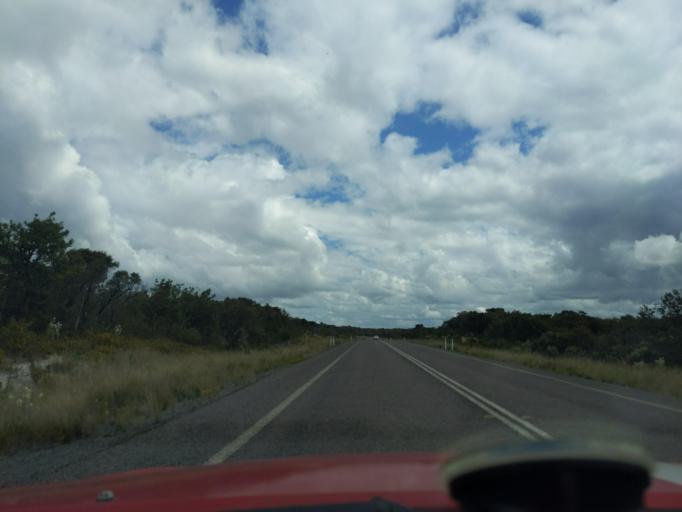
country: AU
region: New South Wales
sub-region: Great Lakes
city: Hawks Nest
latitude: -32.5940
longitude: 152.2560
